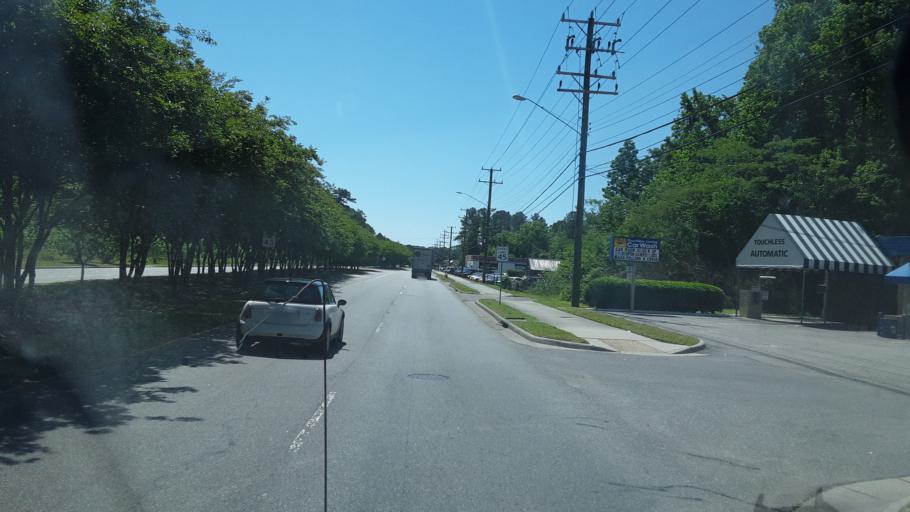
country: US
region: Virginia
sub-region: City of Virginia Beach
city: Virginia Beach
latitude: 36.7956
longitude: -75.9997
